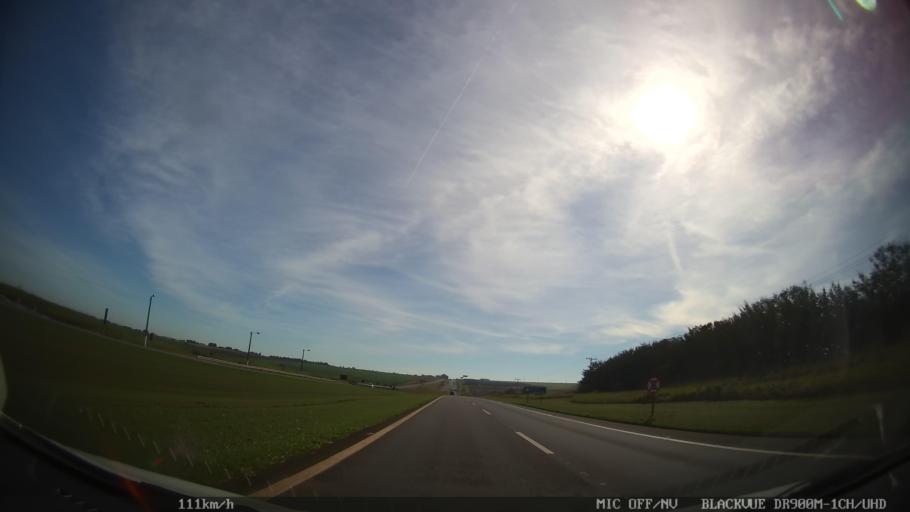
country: BR
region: Sao Paulo
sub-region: Cordeiropolis
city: Cordeiropolis
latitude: -22.4859
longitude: -47.3991
